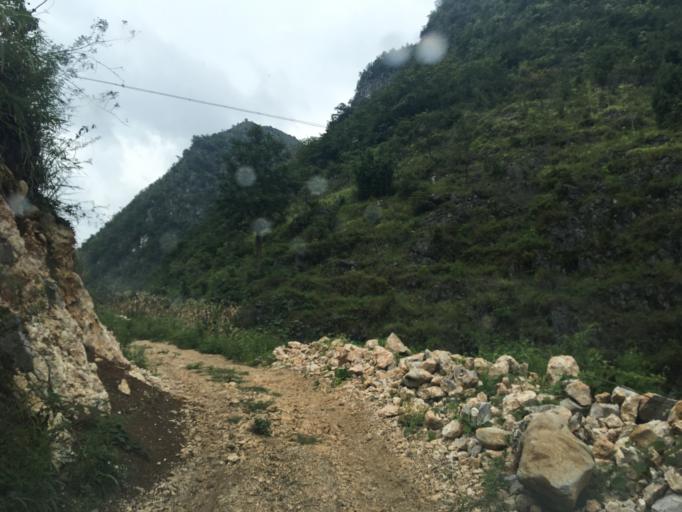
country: CN
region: Guangxi Zhuangzu Zizhiqu
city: Xinzhou
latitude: 25.2179
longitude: 105.6280
